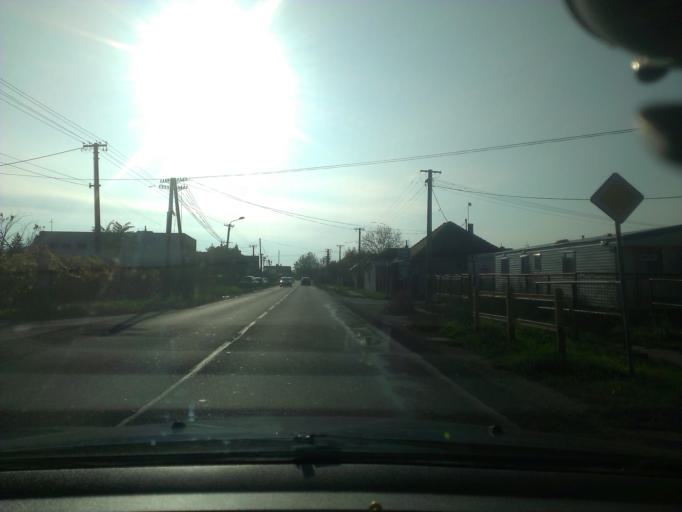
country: SK
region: Nitriansky
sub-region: Okres Nitra
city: Nitra
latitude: 48.3515
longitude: 18.0546
